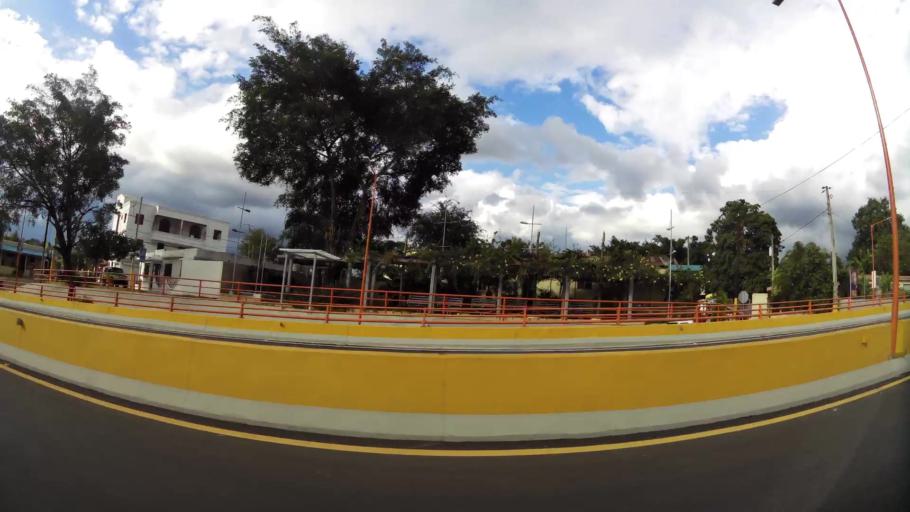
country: DO
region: Monsenor Nouel
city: Piedra Blanca
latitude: 18.8451
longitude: -70.3175
